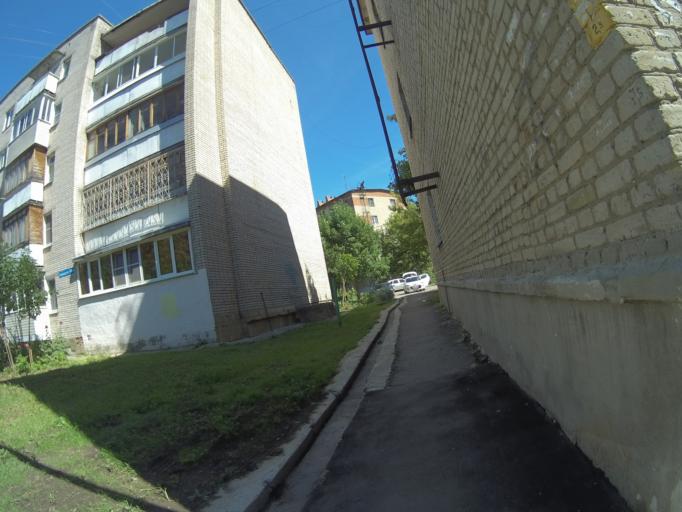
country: RU
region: Vladimir
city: Vladimir
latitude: 56.1303
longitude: 40.3603
